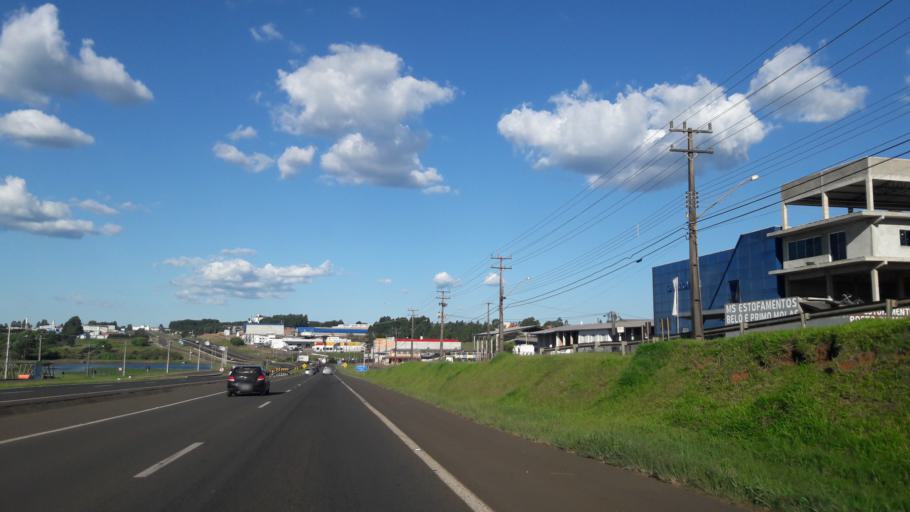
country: BR
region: Parana
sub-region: Guarapuava
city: Guarapuava
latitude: -25.3596
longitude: -51.4668
